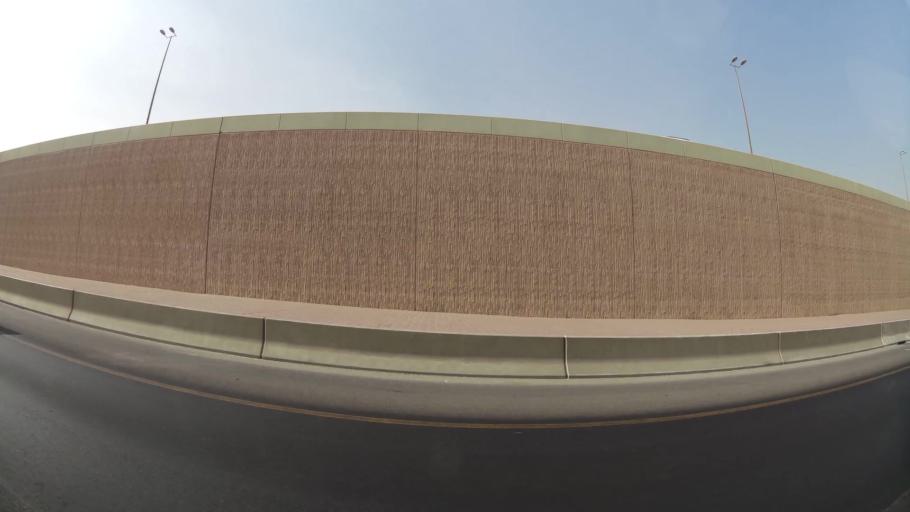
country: KW
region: Al Farwaniyah
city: Al Farwaniyah
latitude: 29.2779
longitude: 47.9498
